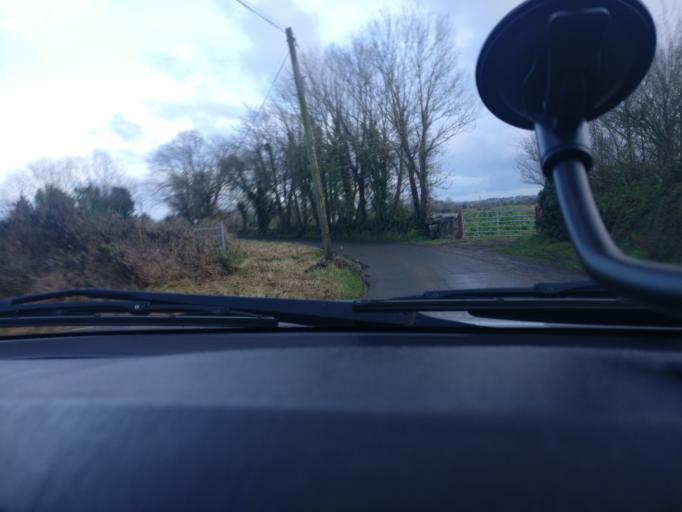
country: IE
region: Connaught
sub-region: County Galway
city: Loughrea
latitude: 53.1974
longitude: -8.6415
